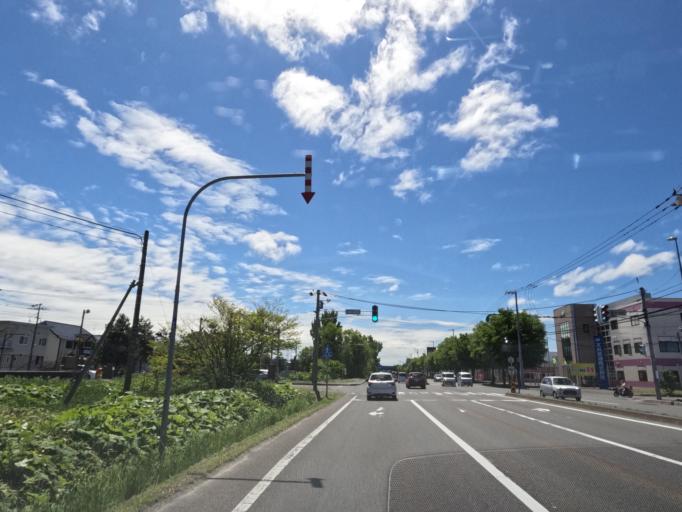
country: JP
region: Hokkaido
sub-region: Asahikawa-shi
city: Asahikawa
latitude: 43.7309
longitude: 142.3655
